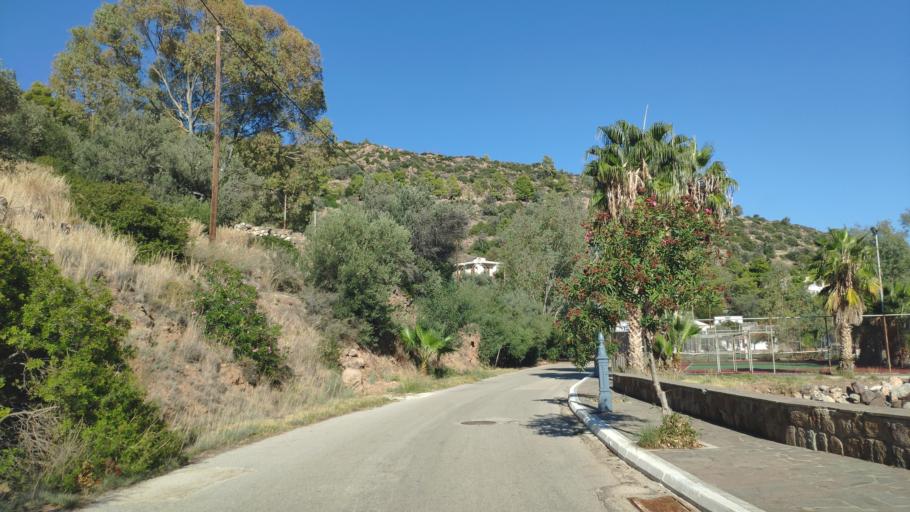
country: GR
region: Attica
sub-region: Nomos Piraios
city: Poros
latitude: 37.5866
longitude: 23.3966
